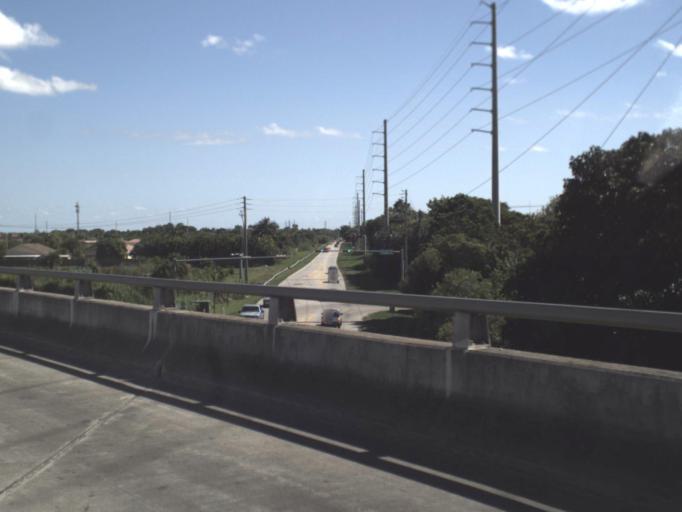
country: US
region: Florida
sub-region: Miami-Dade County
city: Homestead
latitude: 25.4625
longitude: -80.4620
